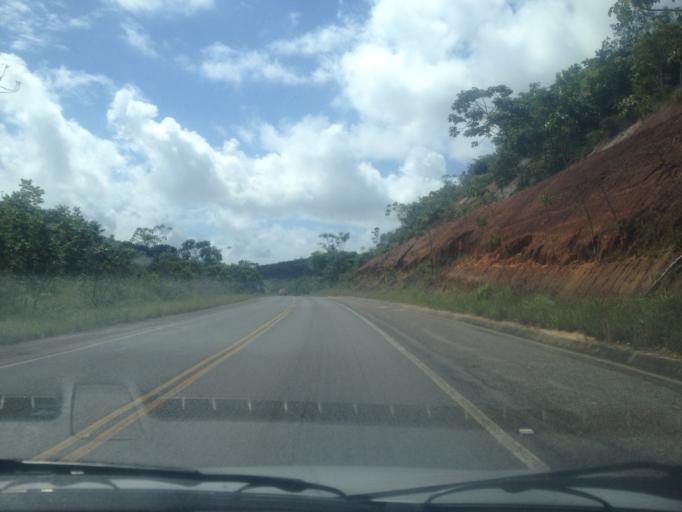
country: BR
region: Bahia
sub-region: Conde
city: Conde
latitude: -12.0332
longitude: -37.7009
